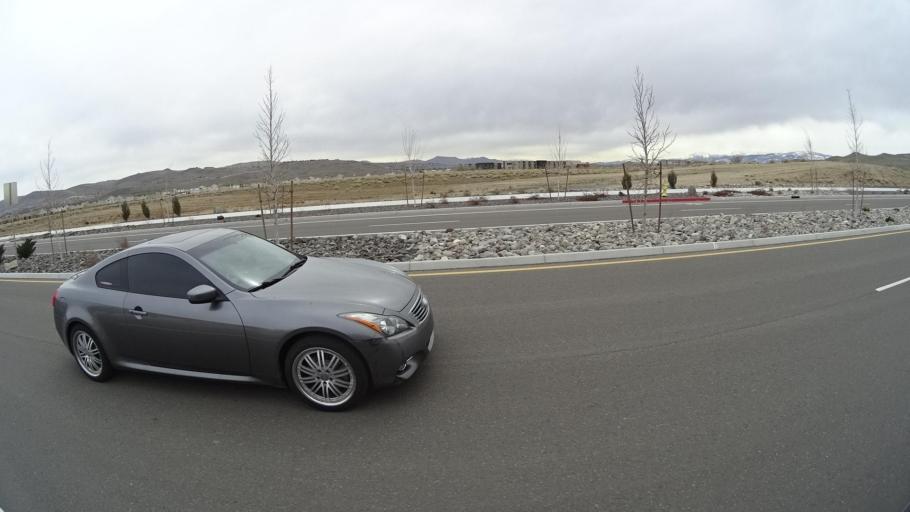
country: US
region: Nevada
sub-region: Washoe County
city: Spanish Springs
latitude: 39.6153
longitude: -119.7218
